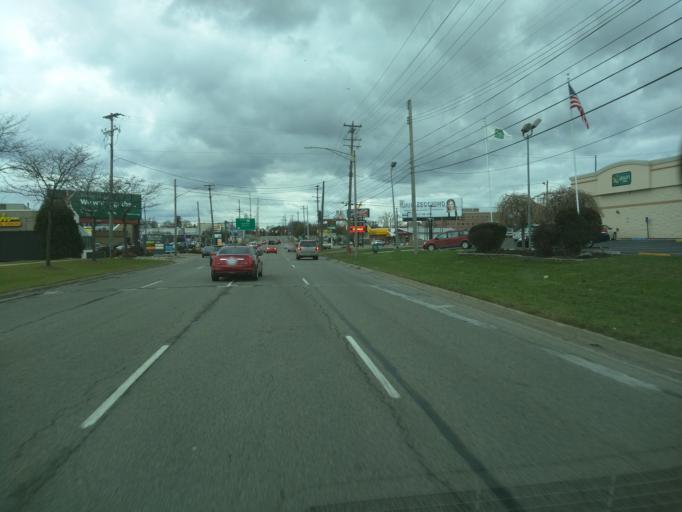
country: US
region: Michigan
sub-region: Ingham County
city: East Lansing
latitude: 42.7415
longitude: -84.5069
